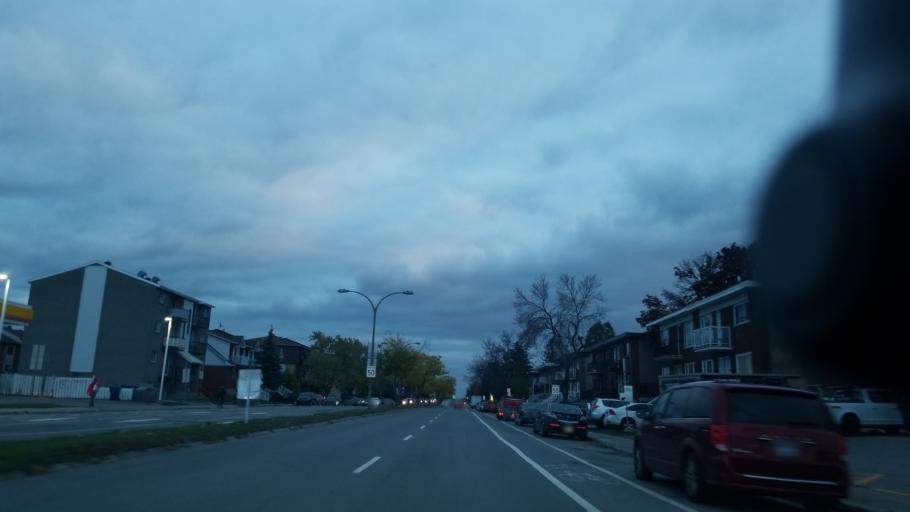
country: CA
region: Quebec
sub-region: Laval
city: Laval
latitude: 45.5640
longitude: -73.7173
